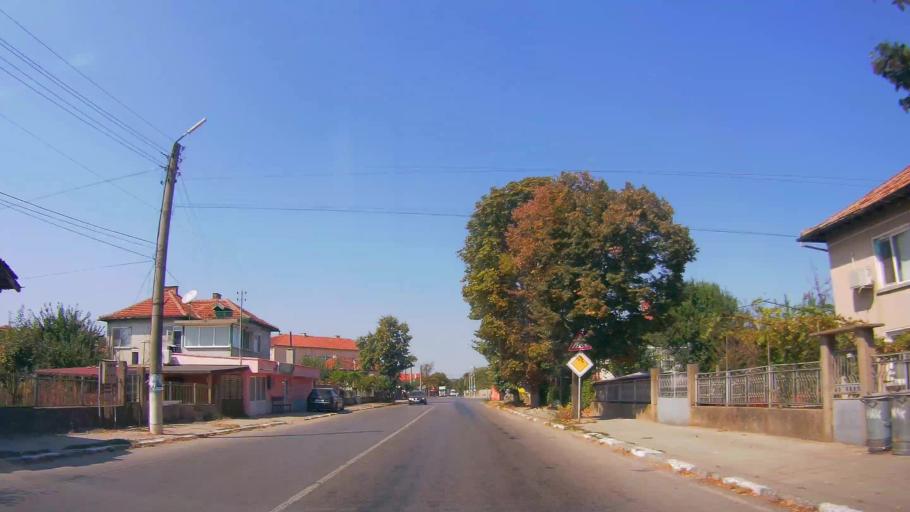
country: BG
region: Razgrad
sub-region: Obshtina Tsar Kaloyan
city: Tsar Kaloyan
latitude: 43.6053
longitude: 26.2411
